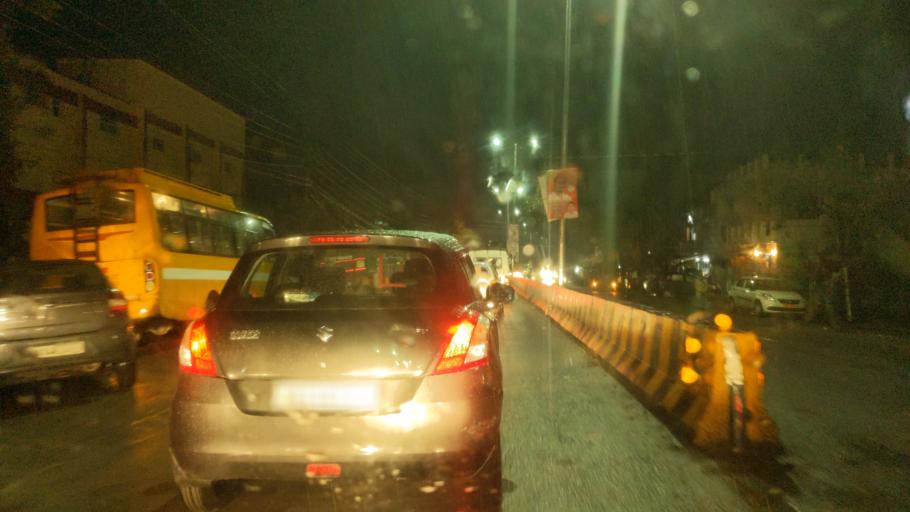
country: IN
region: Uttarakhand
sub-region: Naini Tal
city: Haldwani
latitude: 29.2524
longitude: 79.5413
